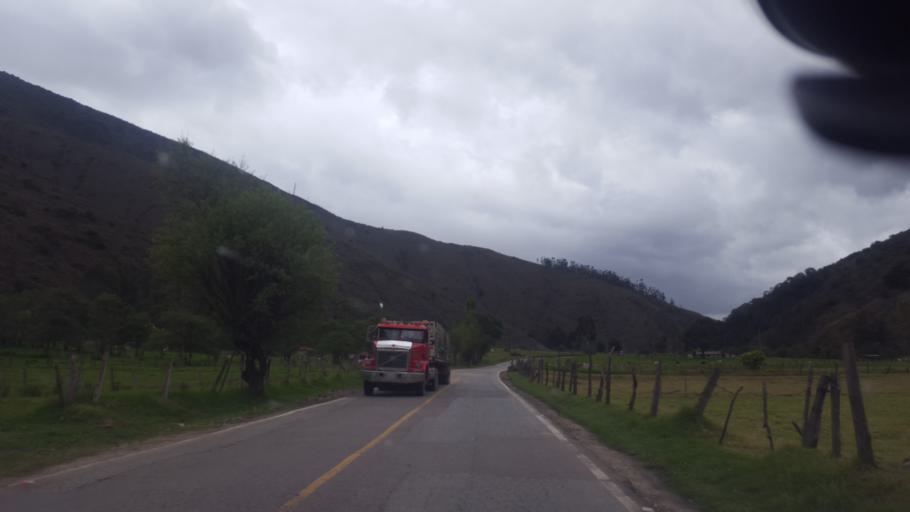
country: CO
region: Boyaca
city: Belen
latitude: 6.0078
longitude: -72.8366
